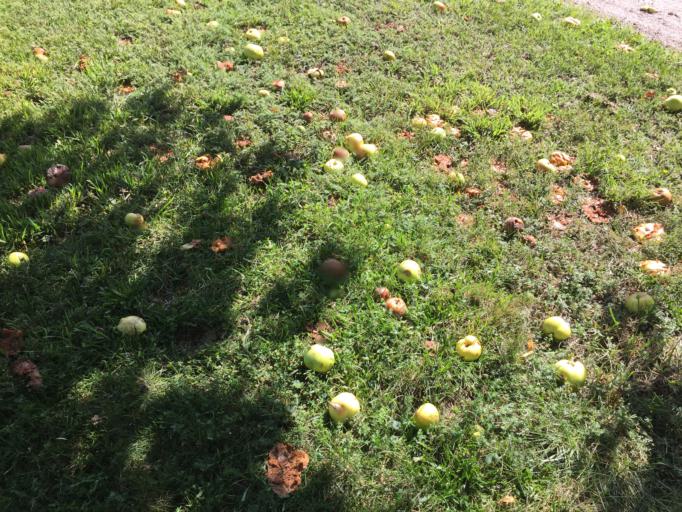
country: SE
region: Soedermanland
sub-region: Vingakers Kommun
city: Vingaker
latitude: 59.1503
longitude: 16.0397
